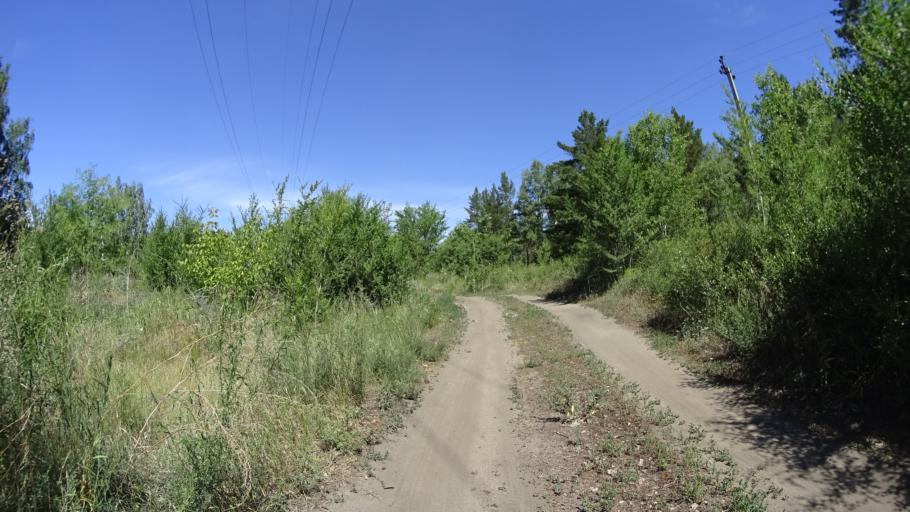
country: RU
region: Chelyabinsk
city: Troitsk
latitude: 54.0535
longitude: 61.6262
